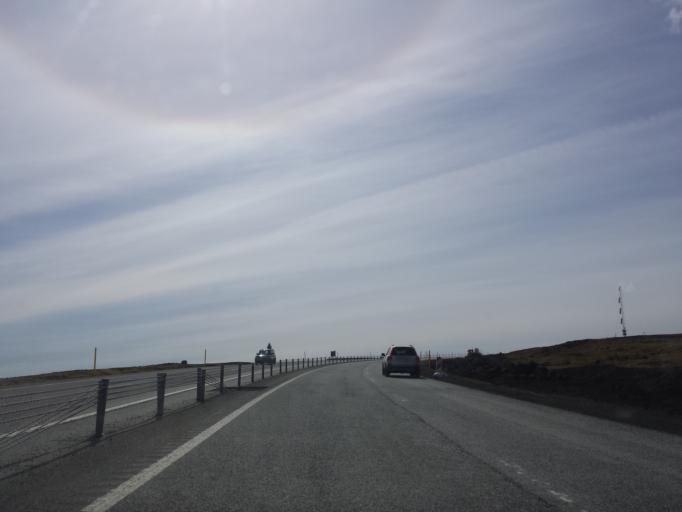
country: IS
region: South
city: Hveragerdi
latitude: 64.0142
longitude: -21.2336
